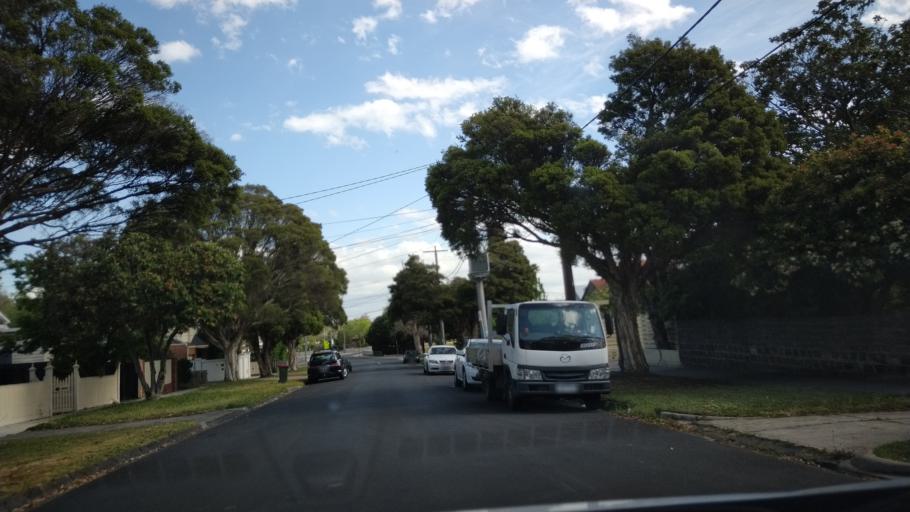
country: AU
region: Victoria
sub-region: Glen Eira
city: Glen Huntly
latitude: -37.8931
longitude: 145.0515
